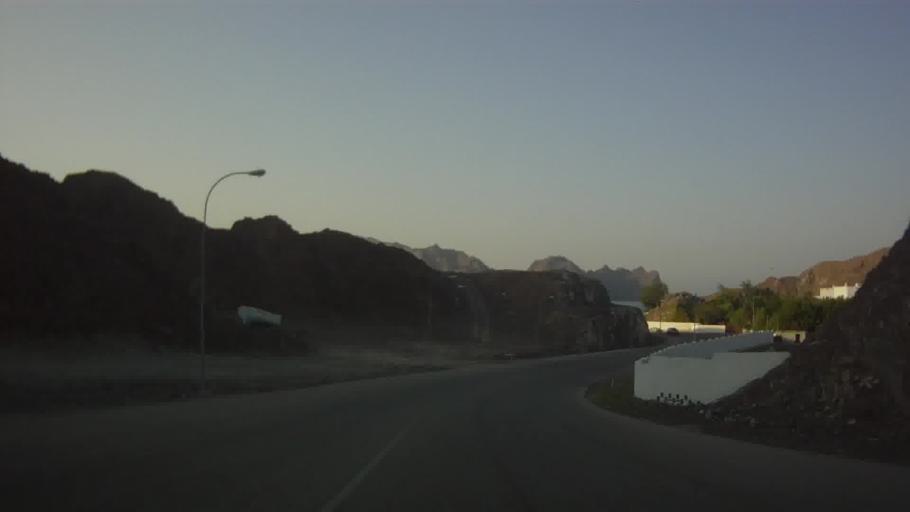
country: OM
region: Muhafazat Masqat
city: Muscat
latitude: 23.5914
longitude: 58.6029
